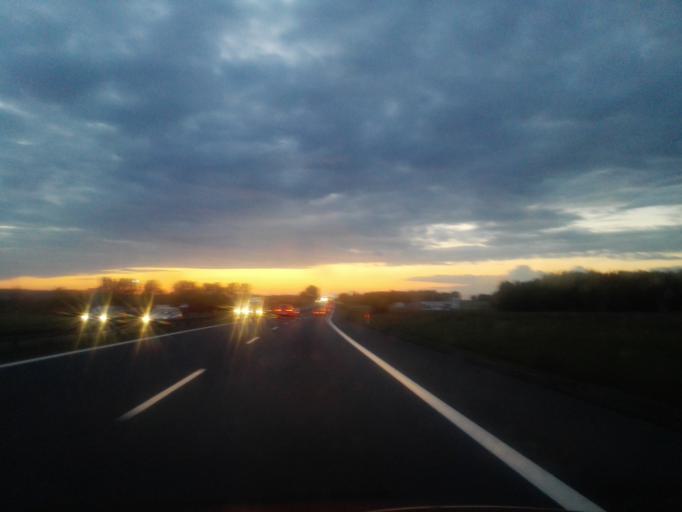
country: PL
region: Lodz Voivodeship
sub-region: Powiat lodzki wschodni
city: Tuszyn
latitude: 51.5565
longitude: 19.5924
